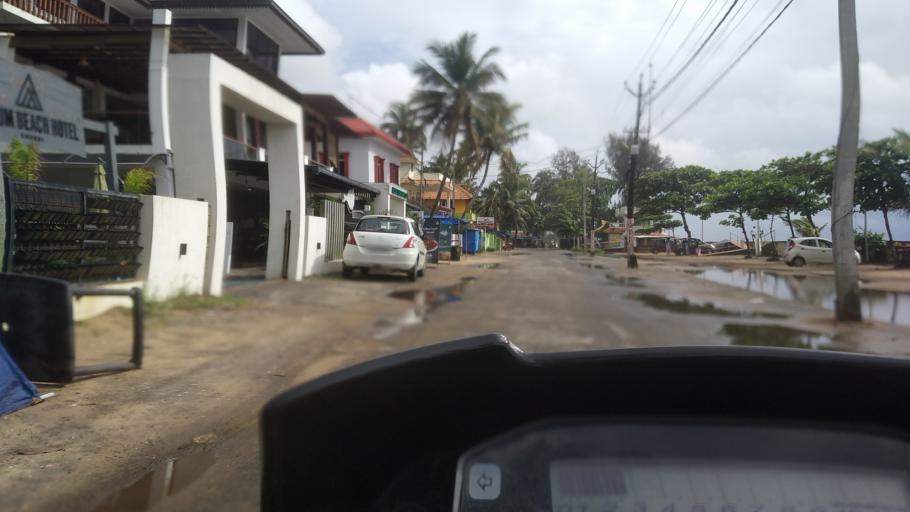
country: IN
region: Kerala
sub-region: Thrissur District
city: Kodungallur
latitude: 10.1403
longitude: 76.1791
